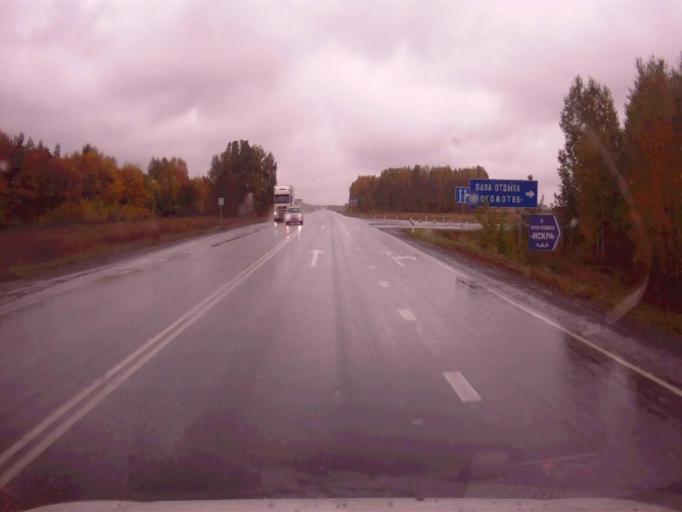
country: RU
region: Chelyabinsk
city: Roshchino
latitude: 55.3953
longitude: 61.0987
